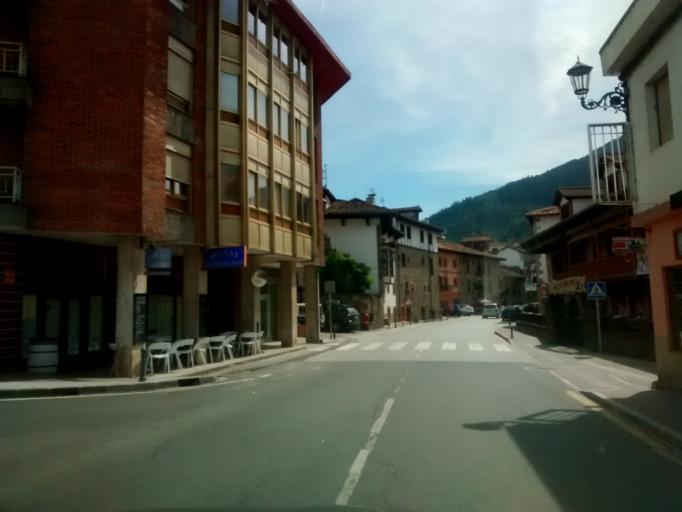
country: ES
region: Cantabria
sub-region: Provincia de Cantabria
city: Potes
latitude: 43.1551
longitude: -4.6204
